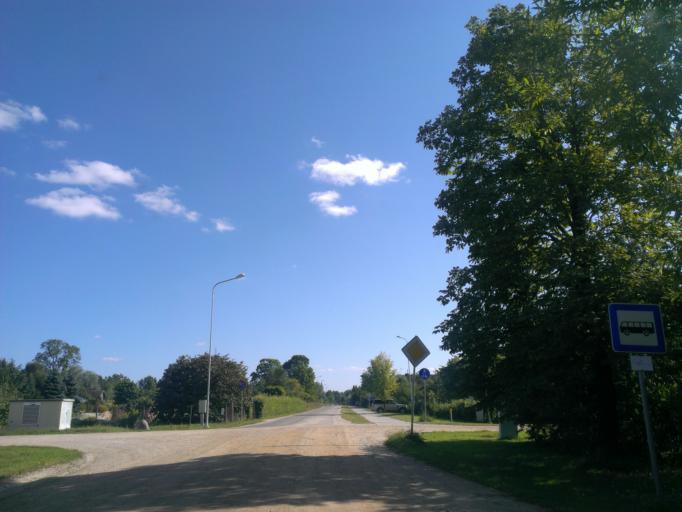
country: LV
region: Sigulda
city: Sigulda
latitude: 57.1629
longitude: 24.8879
